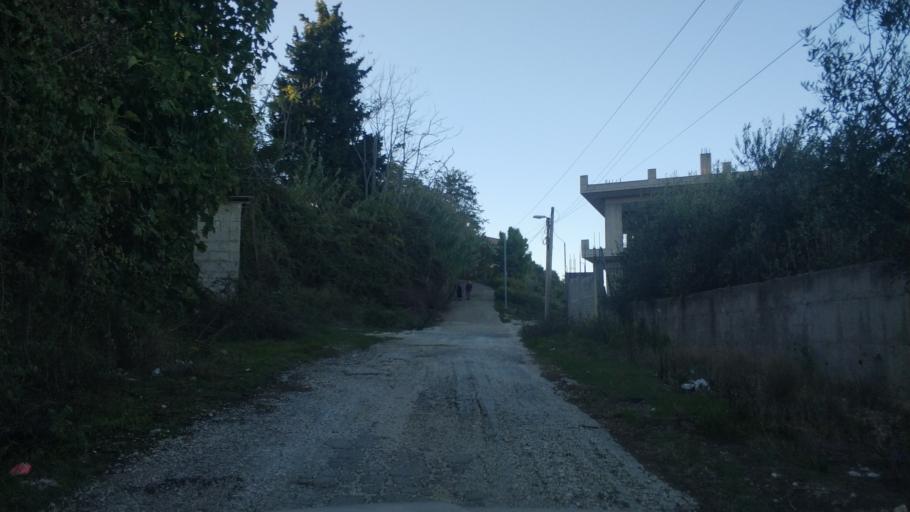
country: AL
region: Vlore
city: Vlore
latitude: 40.5142
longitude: 19.4188
